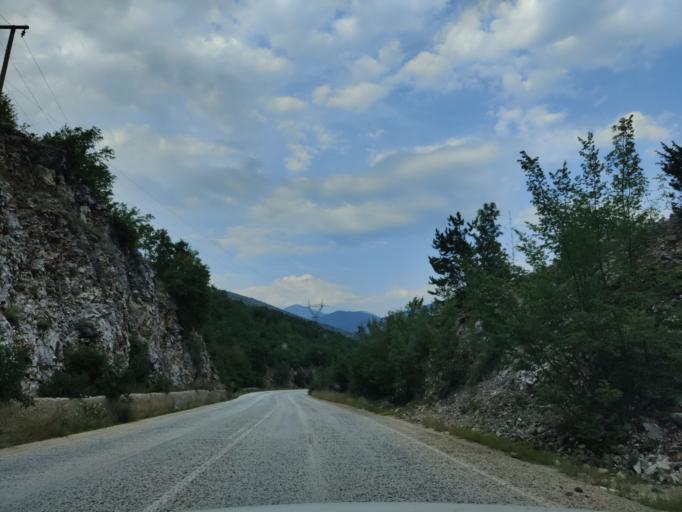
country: GR
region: East Macedonia and Thrace
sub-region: Nomos Dramas
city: Volakas
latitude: 41.2922
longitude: 23.9511
